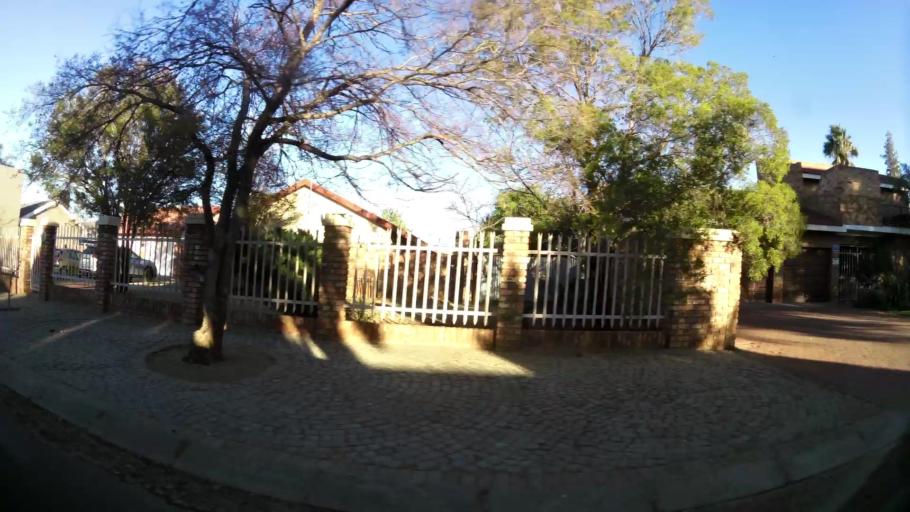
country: ZA
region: Northern Cape
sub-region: Frances Baard District Municipality
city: Kimberley
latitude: -28.7588
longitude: 24.7560
